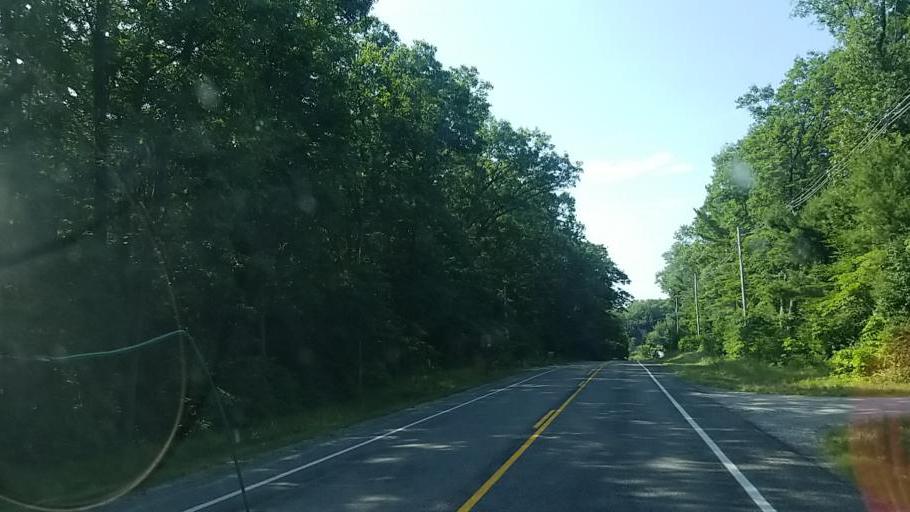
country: US
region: Michigan
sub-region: Muskegon County
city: Whitehall
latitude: 43.3472
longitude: -86.3764
